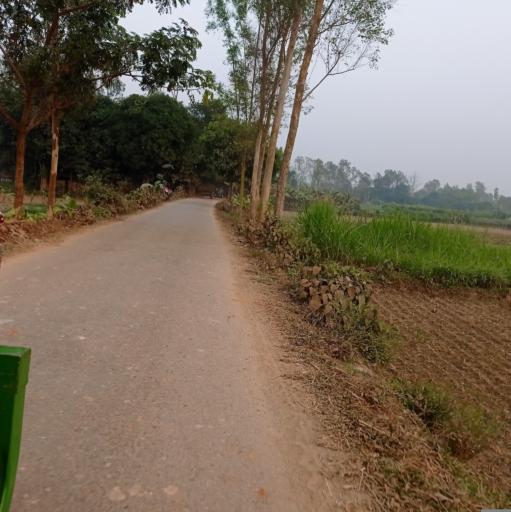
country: BD
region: Dhaka
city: Bajitpur
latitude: 24.1306
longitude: 90.8220
